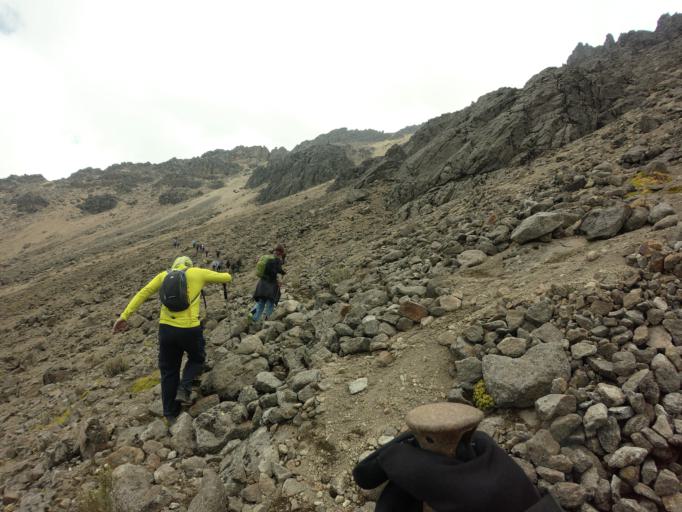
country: MX
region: Mexico
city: Amecameca de Juarez
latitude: 19.1504
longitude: -98.6384
